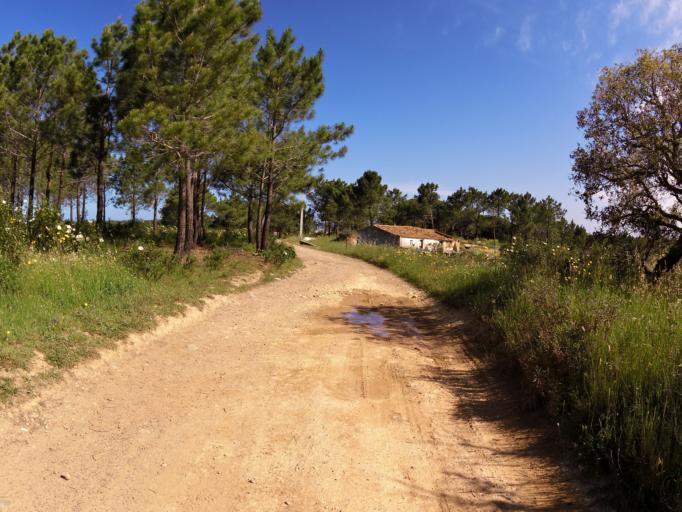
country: PT
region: Faro
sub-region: Aljezur
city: Aljezur
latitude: 37.3335
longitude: -8.8085
